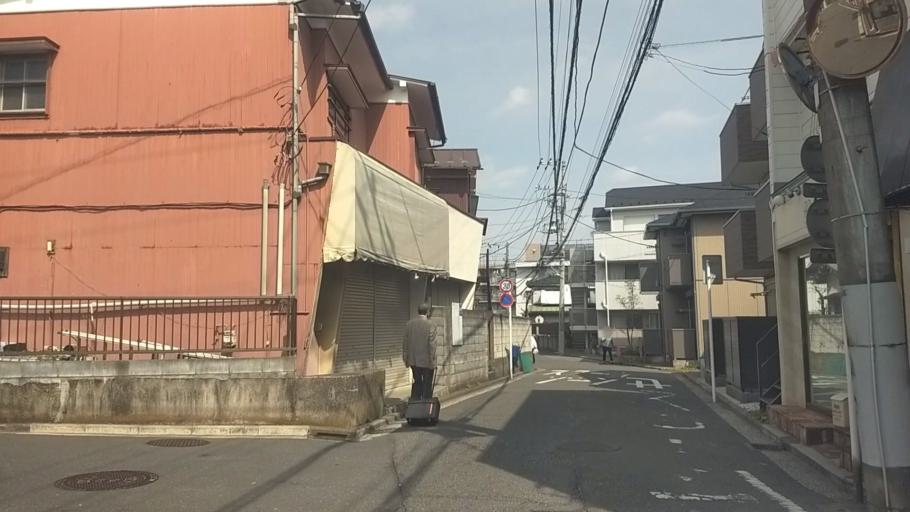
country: JP
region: Kanagawa
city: Yokohama
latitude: 35.3809
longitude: 139.6170
